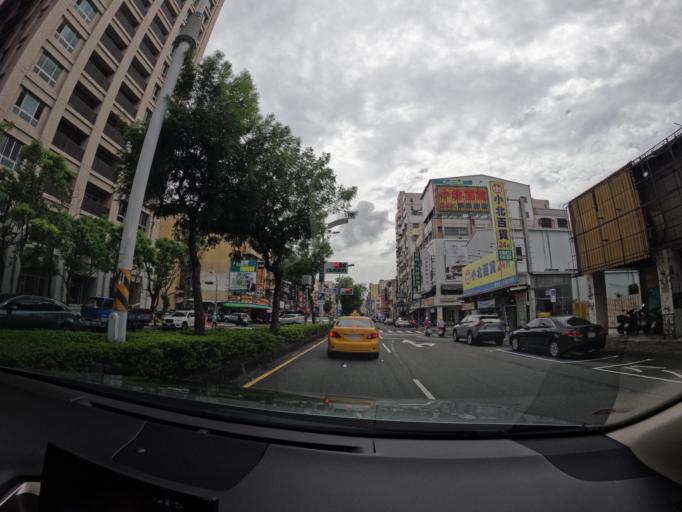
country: TW
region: Kaohsiung
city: Kaohsiung
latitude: 22.6400
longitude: 120.3200
